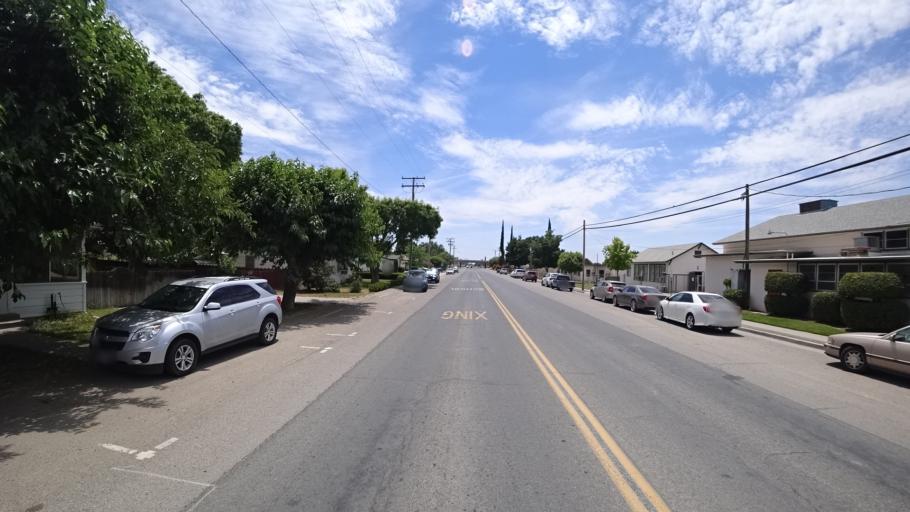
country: US
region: California
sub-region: Kings County
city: Armona
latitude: 36.3119
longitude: -119.7091
